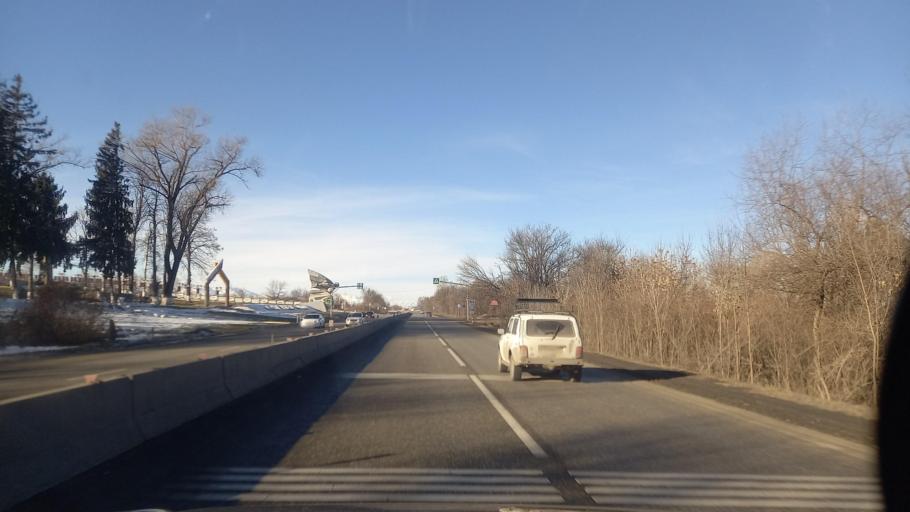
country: RU
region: North Ossetia
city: Gizel'
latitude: 43.0287
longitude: 44.5877
